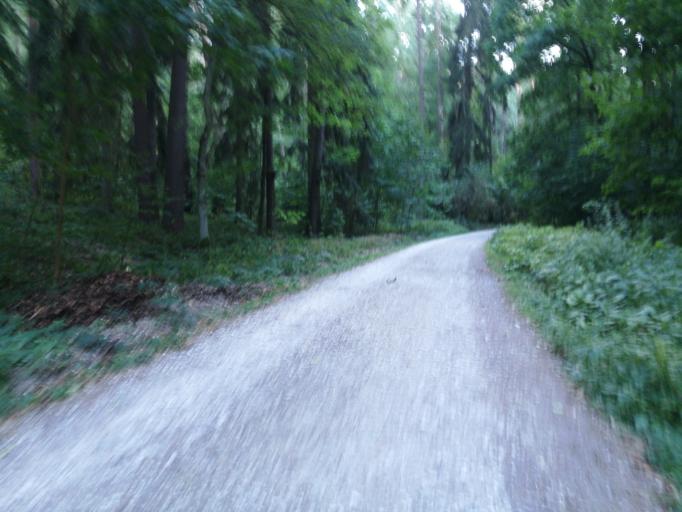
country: DE
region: Bavaria
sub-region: Regierungsbezirk Mittelfranken
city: Seukendorf
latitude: 49.4754
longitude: 10.9226
